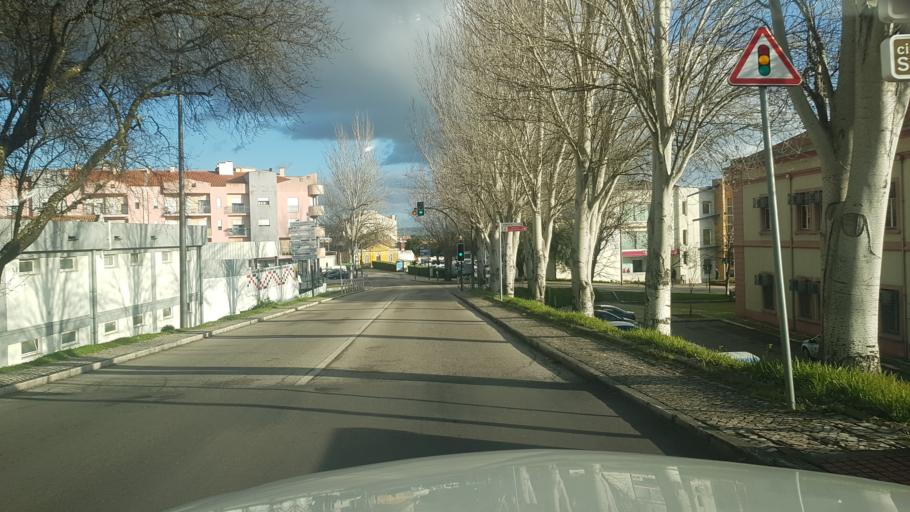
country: PT
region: Santarem
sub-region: Entroncamento
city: Entroncamento
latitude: 39.4659
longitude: -8.4686
